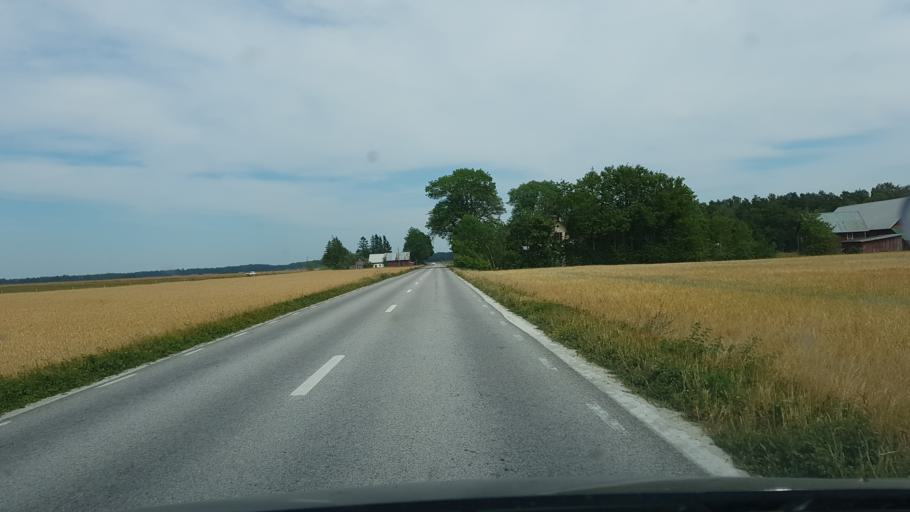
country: SE
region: Gotland
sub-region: Gotland
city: Visby
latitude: 57.7080
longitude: 18.5348
